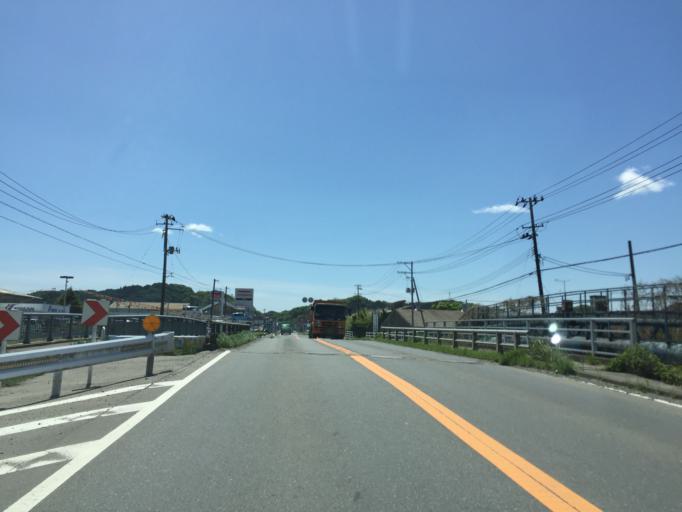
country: JP
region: Fukushima
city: Iwaki
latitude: 36.9825
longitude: 140.8699
